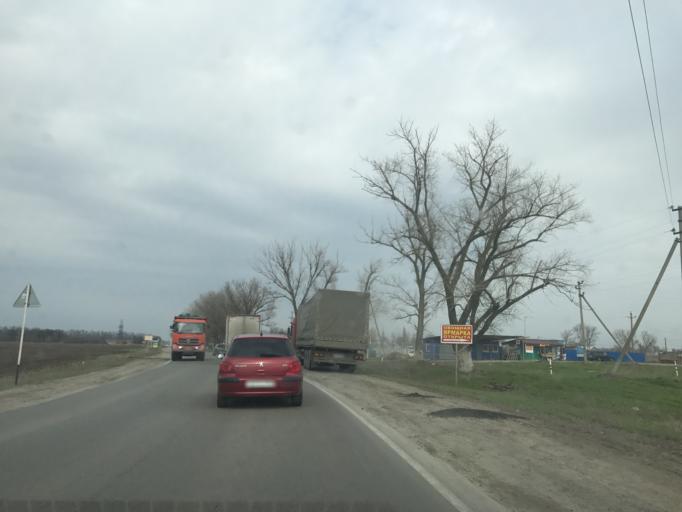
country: RU
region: Rostov
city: Starocherkasskaya
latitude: 47.3179
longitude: 39.9661
